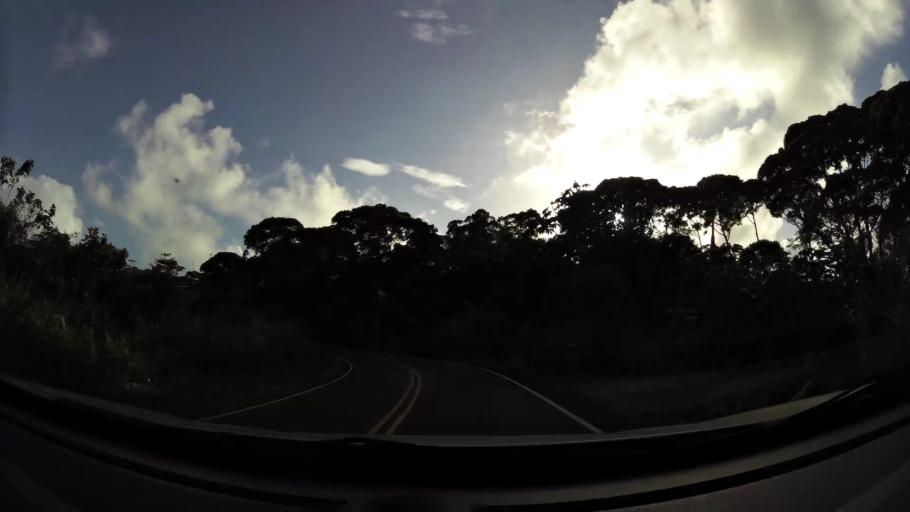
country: CR
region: Limon
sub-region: Canton de Siquirres
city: Siquirres
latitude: 10.0617
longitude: -83.5538
